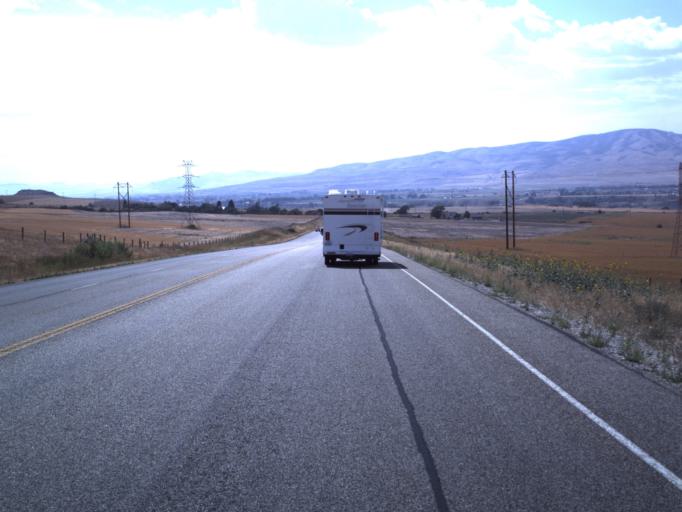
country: US
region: Utah
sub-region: Box Elder County
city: Garland
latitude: 41.7922
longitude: -112.0660
